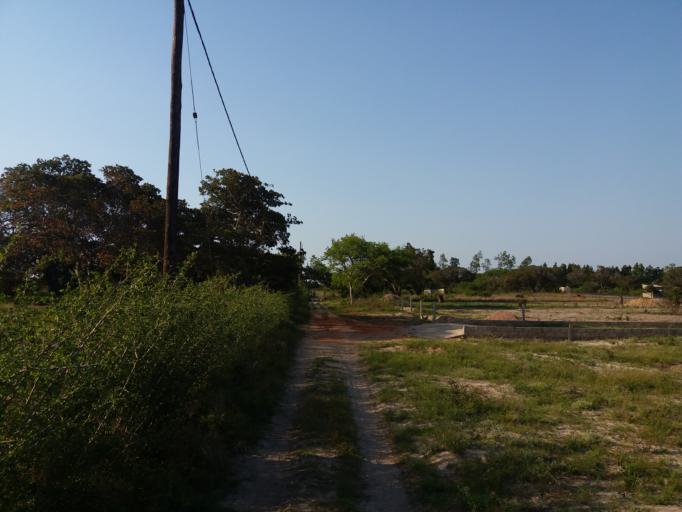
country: MZ
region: Maputo City
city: Maputo
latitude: -25.7604
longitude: 32.6076
